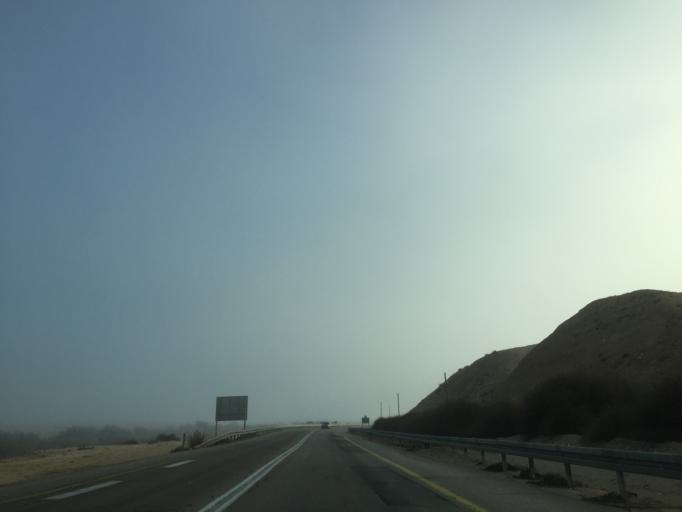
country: IL
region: Southern District
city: Yeroham
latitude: 30.9944
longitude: 34.9186
